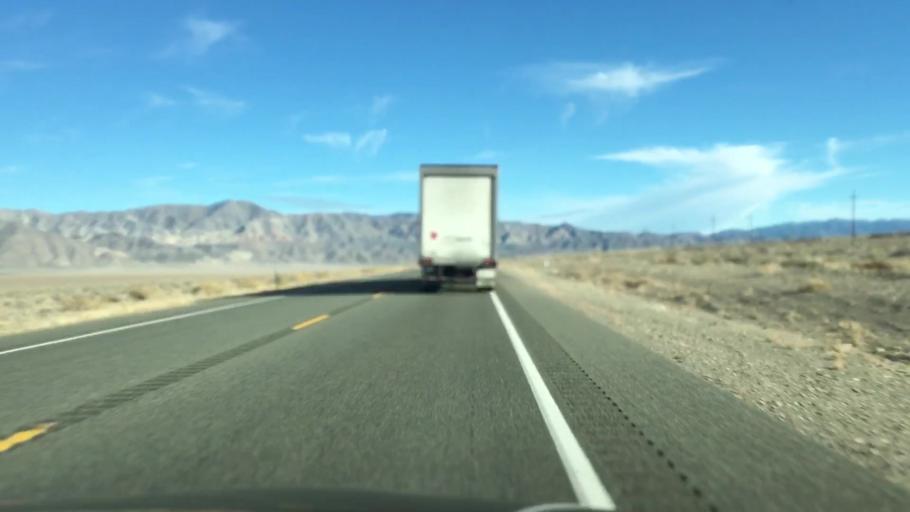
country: US
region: Nevada
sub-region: Mineral County
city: Hawthorne
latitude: 38.5281
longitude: -118.2411
